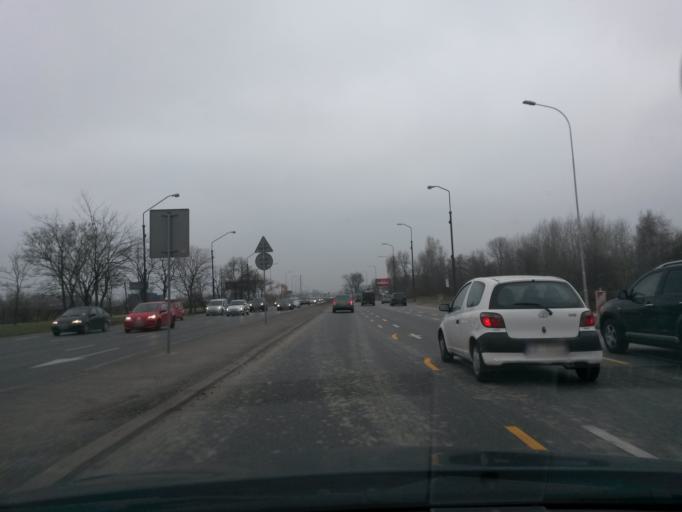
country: PL
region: Masovian Voivodeship
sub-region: Powiat piaseczynski
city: Mysiadlo
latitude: 52.1054
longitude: 21.0185
